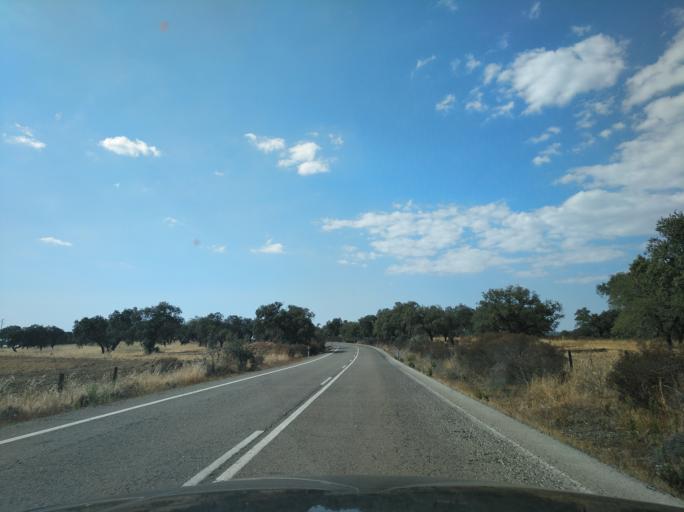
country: ES
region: Andalusia
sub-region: Provincia de Huelva
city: Santa Barbara de Casa
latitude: 37.7662
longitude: -7.1383
